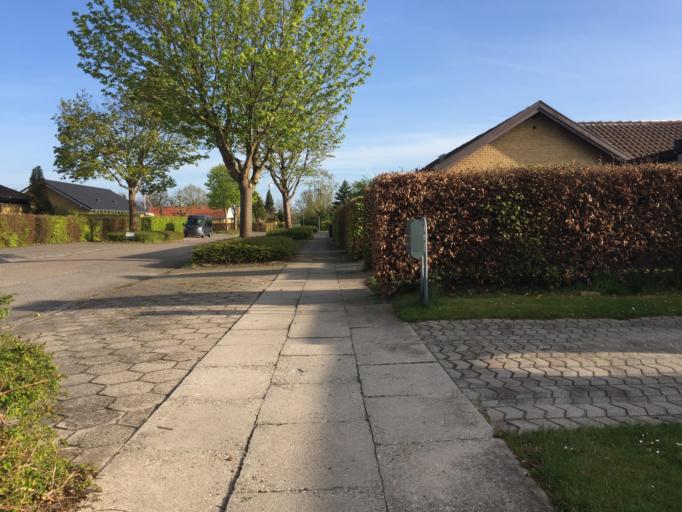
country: DK
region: South Denmark
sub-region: Odense Kommune
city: Odense
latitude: 55.3756
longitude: 10.4140
